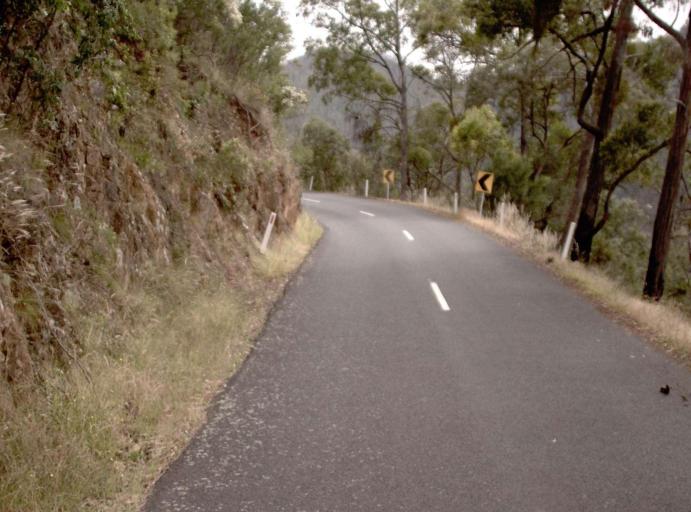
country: AU
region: Victoria
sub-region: Wellington
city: Heyfield
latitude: -37.7391
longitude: 146.6701
